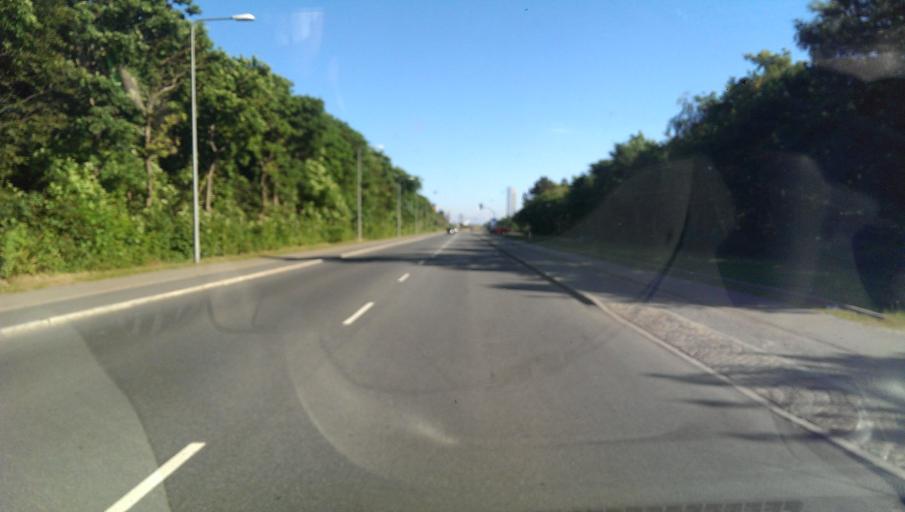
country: DK
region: South Denmark
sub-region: Esbjerg Kommune
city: Esbjerg
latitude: 55.4918
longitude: 8.4110
